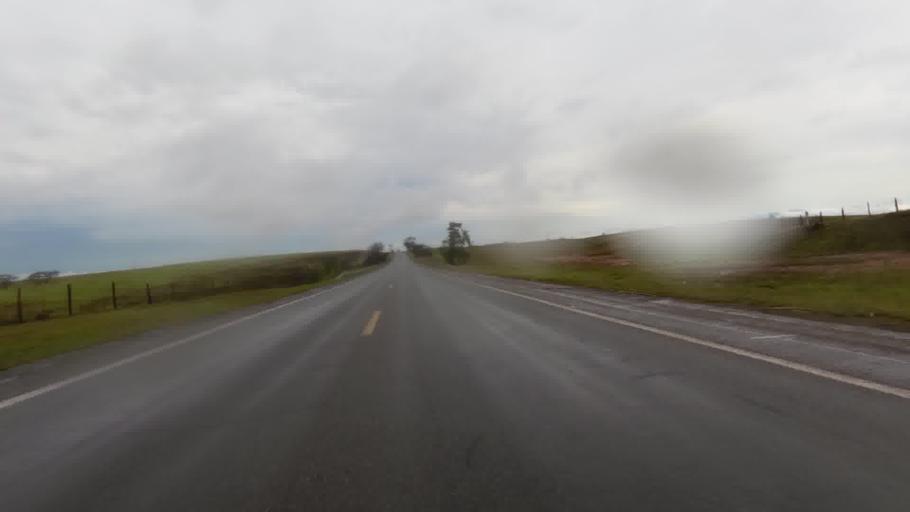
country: BR
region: Rio de Janeiro
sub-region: Campos Dos Goytacazes
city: Campos
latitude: -21.5203
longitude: -41.3346
